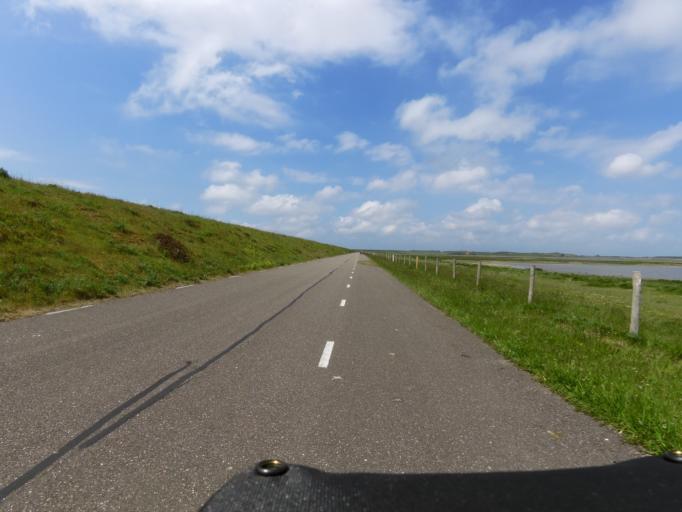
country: NL
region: Zeeland
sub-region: Schouwen-Duiveland
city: Scharendijke
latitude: 51.6839
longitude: 3.8374
